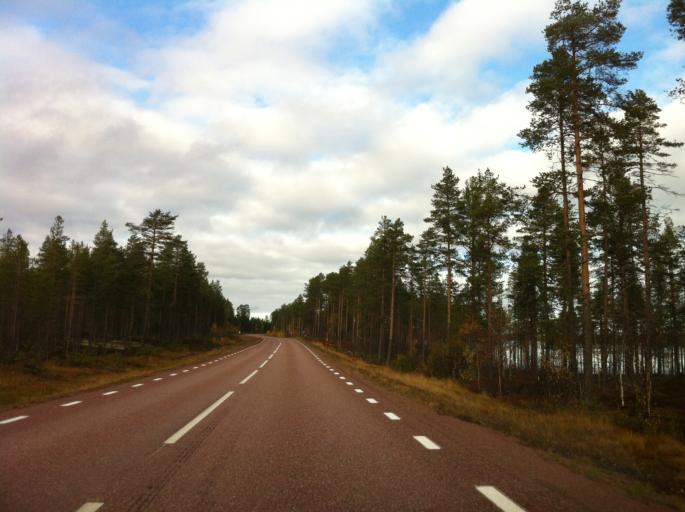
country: SE
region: Dalarna
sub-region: Alvdalens Kommun
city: AElvdalen
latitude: 61.5400
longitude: 13.3438
